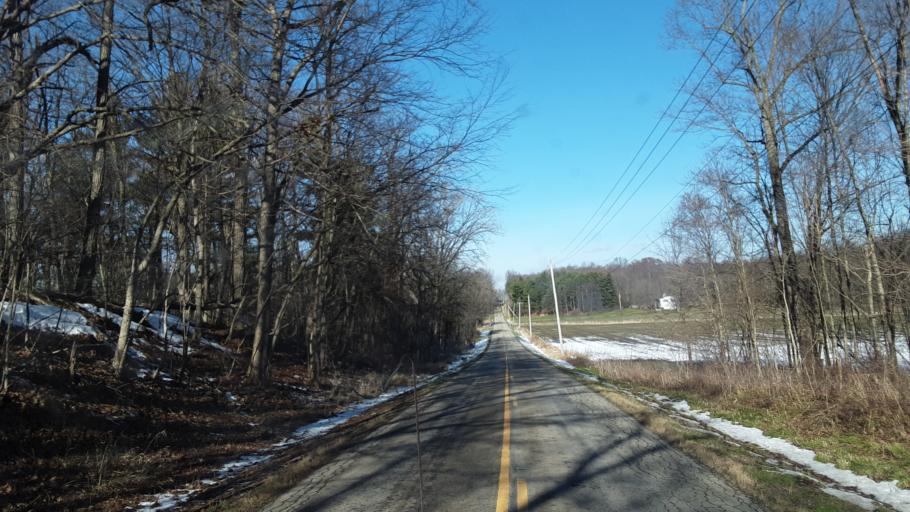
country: US
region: Ohio
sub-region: Richland County
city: Lincoln Heights
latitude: 40.8465
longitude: -82.4789
